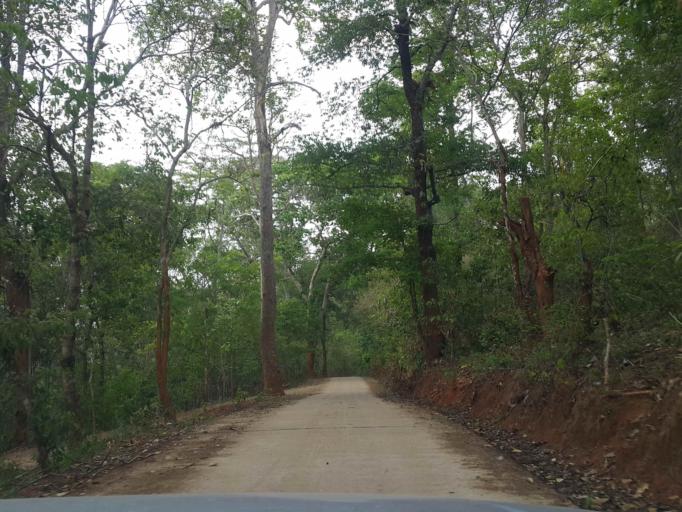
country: TH
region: Chiang Mai
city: Wiang Haeng
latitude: 19.3710
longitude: 98.7192
